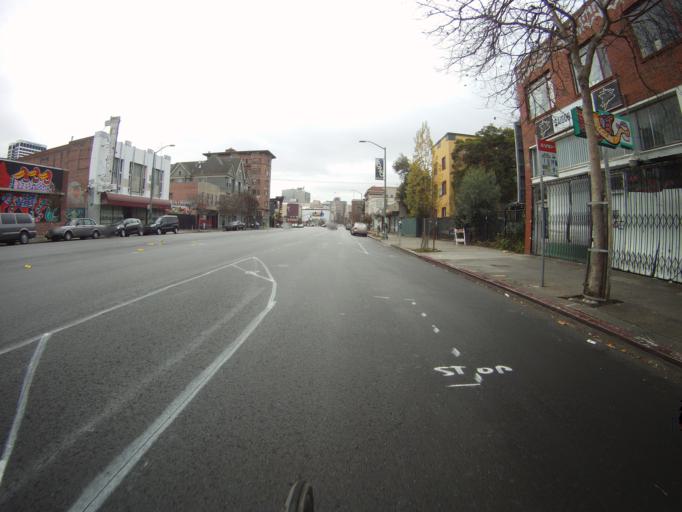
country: US
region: California
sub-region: Alameda County
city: Oakland
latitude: 37.8131
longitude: -122.2688
